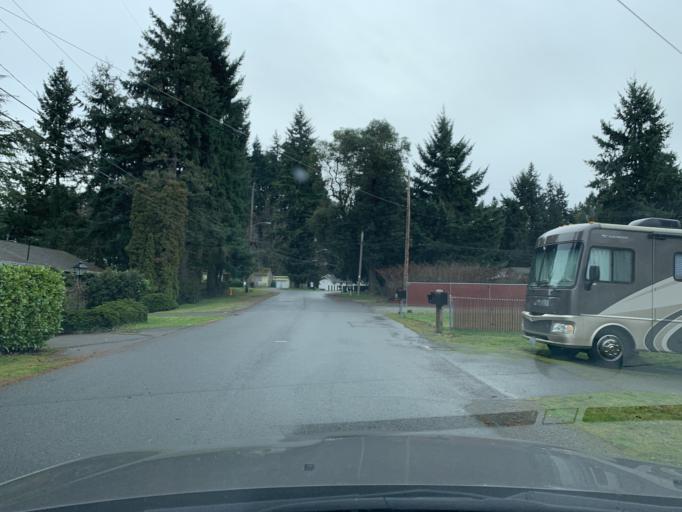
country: US
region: Washington
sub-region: King County
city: SeaTac
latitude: 47.4628
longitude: -122.2785
